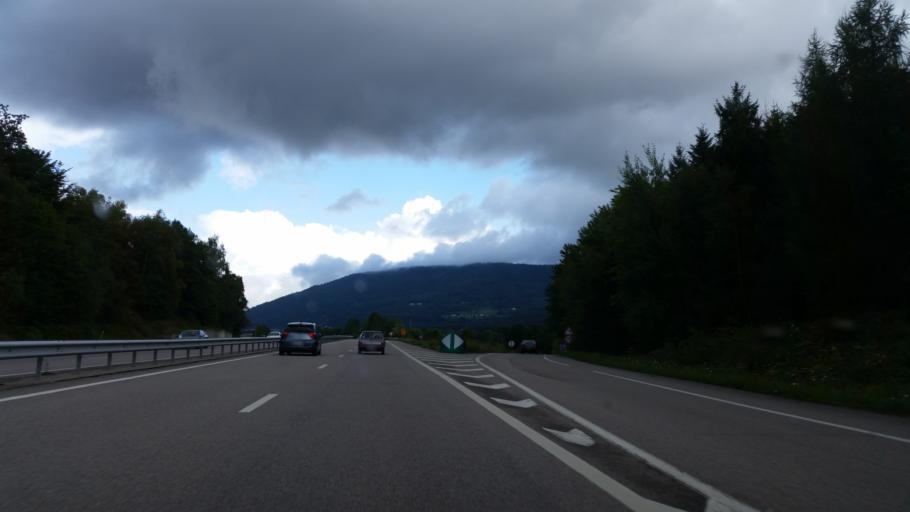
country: FR
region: Lorraine
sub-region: Departement des Vosges
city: Dommartin-les-Remiremont
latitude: 47.9965
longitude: 6.6197
